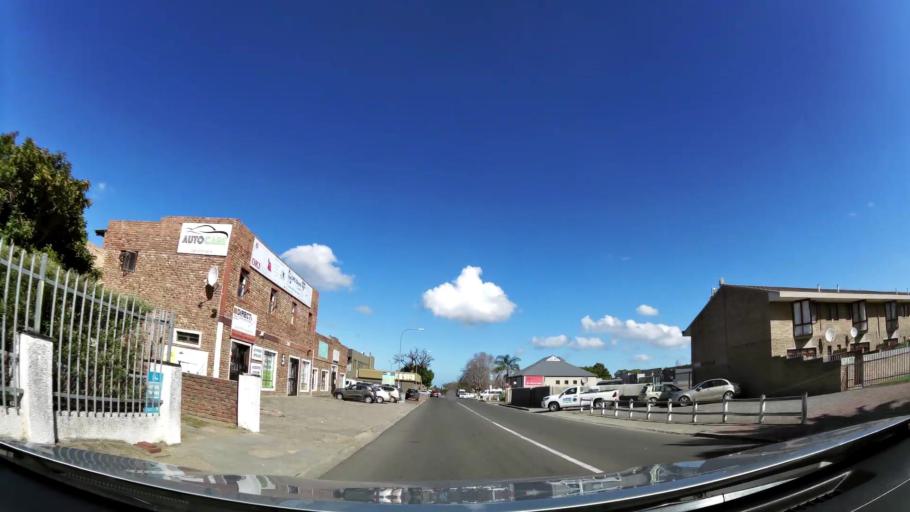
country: ZA
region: Western Cape
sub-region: Eden District Municipality
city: George
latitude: -33.9573
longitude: 22.4652
